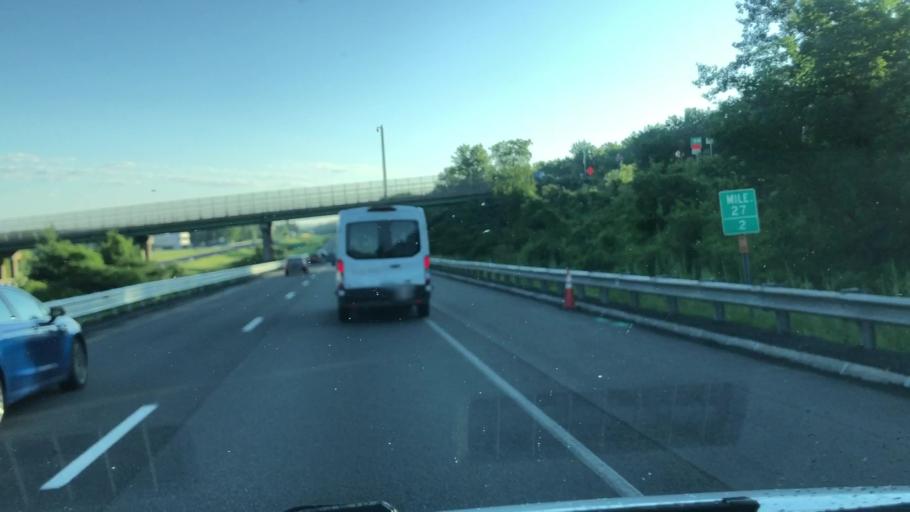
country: US
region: Massachusetts
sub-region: Hampshire County
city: Northampton
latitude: 42.3594
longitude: -72.6368
